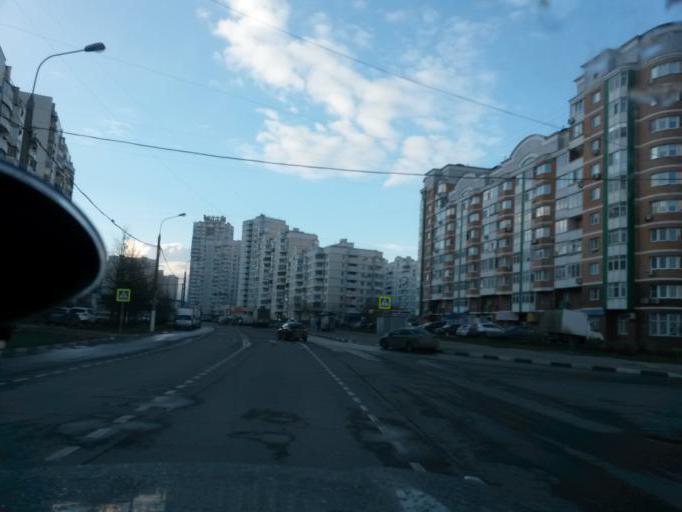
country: RU
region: Moskovskaya
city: Shcherbinka
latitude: 55.5435
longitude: 37.5581
